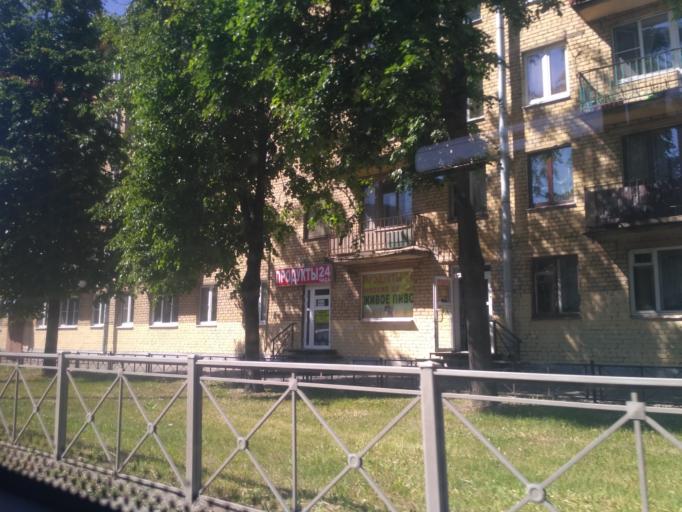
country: RU
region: Leningrad
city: Kalininskiy
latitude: 59.9603
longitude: 30.4223
